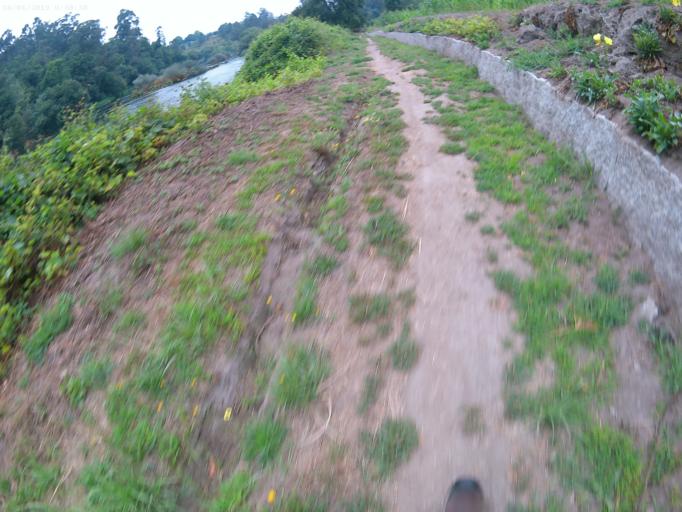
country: PT
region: Viana do Castelo
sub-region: Ponte da Barca
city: Ponte da Barca
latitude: 41.8026
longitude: -8.4696
